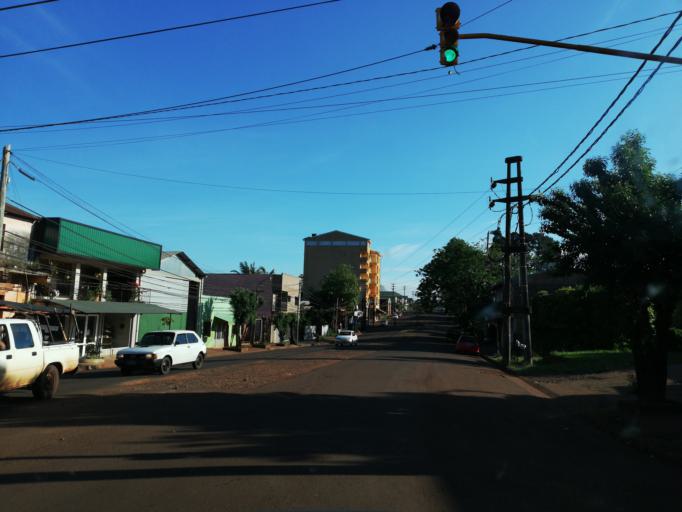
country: AR
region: Misiones
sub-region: Departamento de Obera
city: Obera
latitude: -27.5022
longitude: -55.1194
